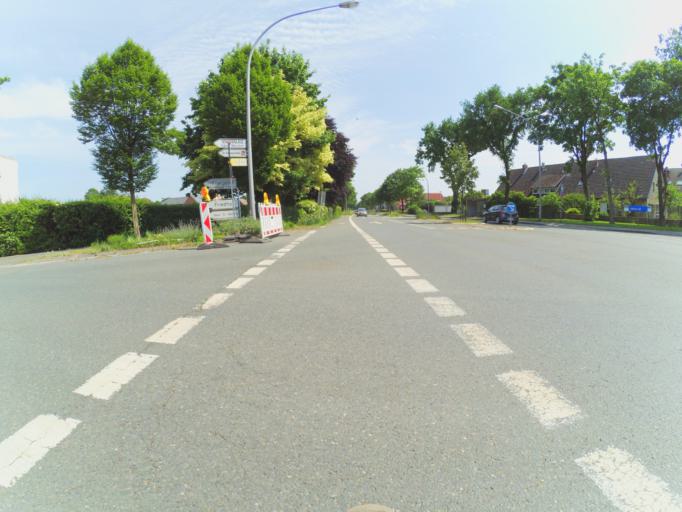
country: DE
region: North Rhine-Westphalia
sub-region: Regierungsbezirk Munster
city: Birgte
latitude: 52.2962
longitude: 7.6588
